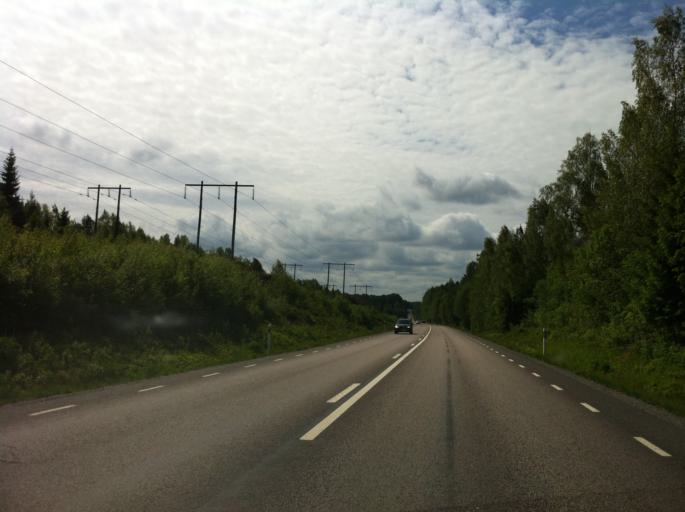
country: SE
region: Vaermland
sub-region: Karlstads Kommun
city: Valberg
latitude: 59.4115
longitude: 13.1835
